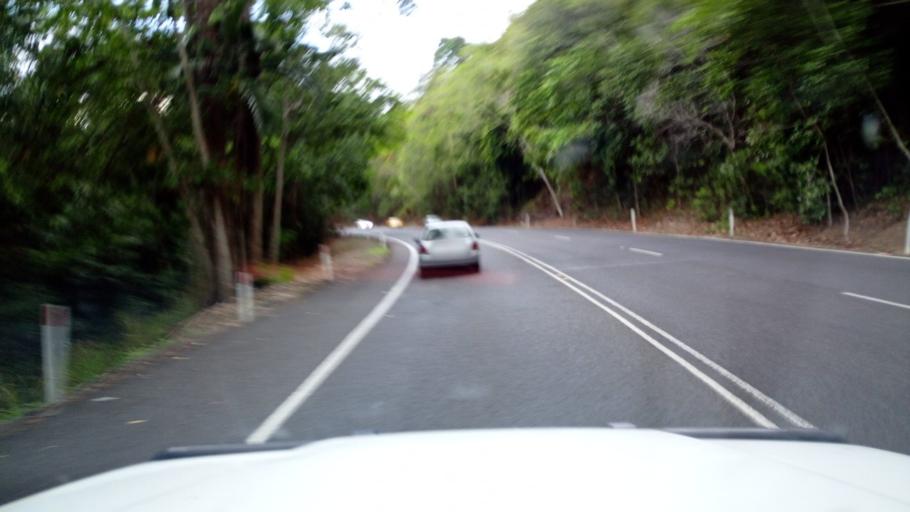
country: AU
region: Queensland
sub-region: Cairns
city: Redlynch
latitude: -16.8499
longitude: 145.6831
